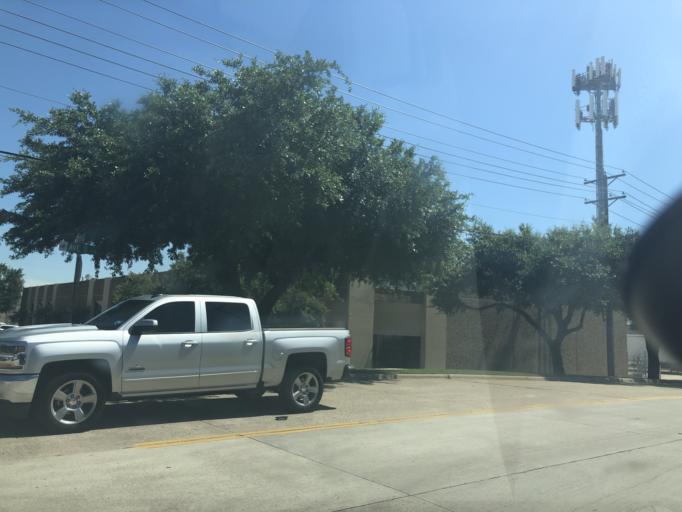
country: US
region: Texas
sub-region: Dallas County
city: Grand Prairie
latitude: 32.7879
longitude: -97.0421
